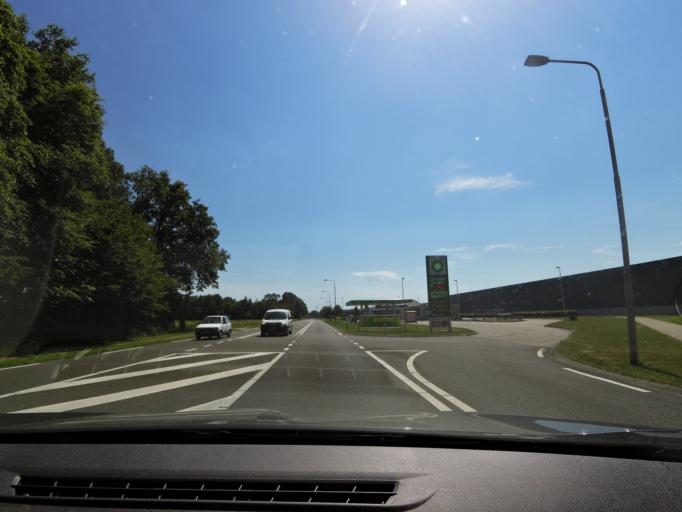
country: NL
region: Gelderland
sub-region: Berkelland
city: Eibergen
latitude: 52.0572
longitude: 6.6275
